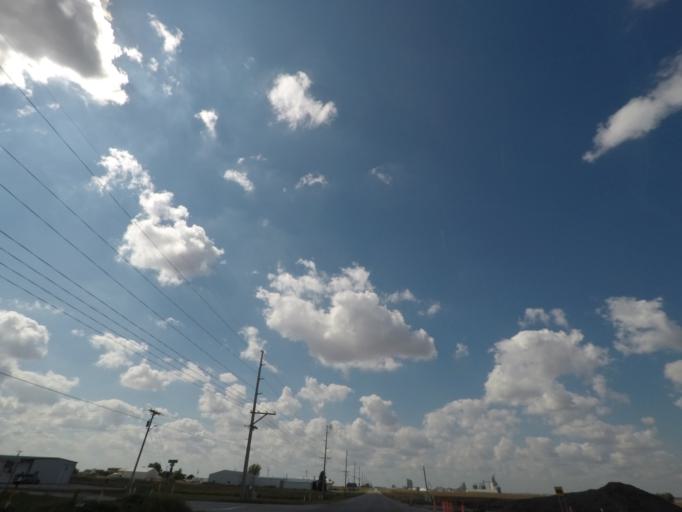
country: US
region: Iowa
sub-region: Story County
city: Nevada
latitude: 42.0230
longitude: -93.4818
